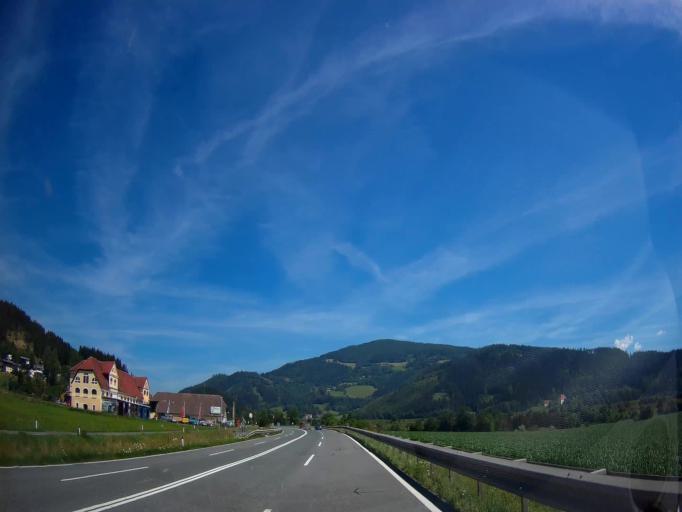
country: AT
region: Carinthia
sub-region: Politischer Bezirk Sankt Veit an der Glan
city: Althofen
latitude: 46.8745
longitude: 14.4504
